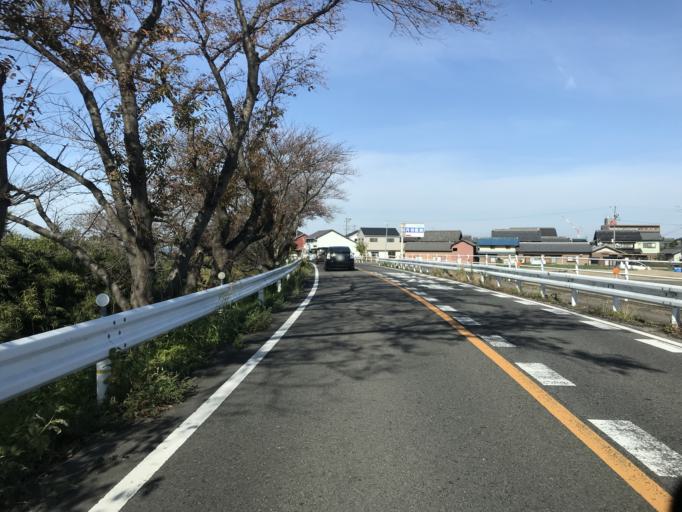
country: JP
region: Aichi
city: Iwakura
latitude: 35.2275
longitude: 136.8463
